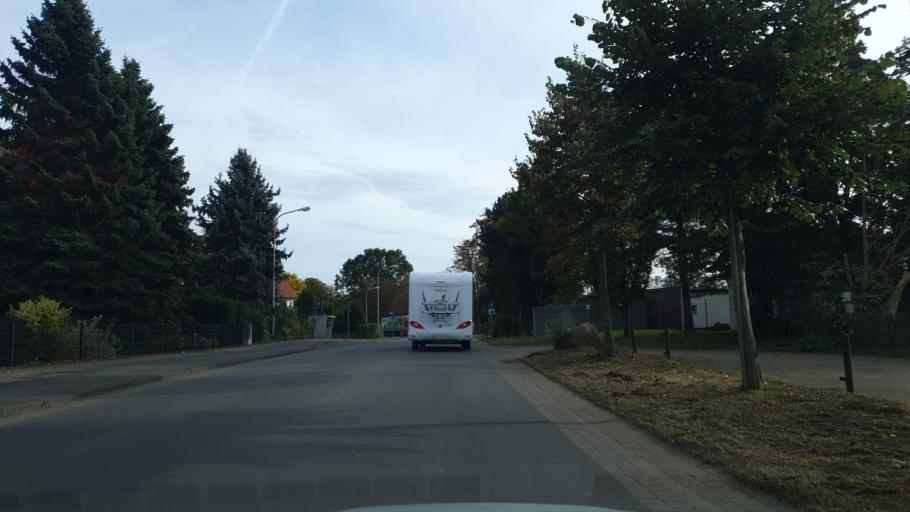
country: DE
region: Lower Saxony
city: Rinteln
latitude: 52.1944
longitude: 9.0724
